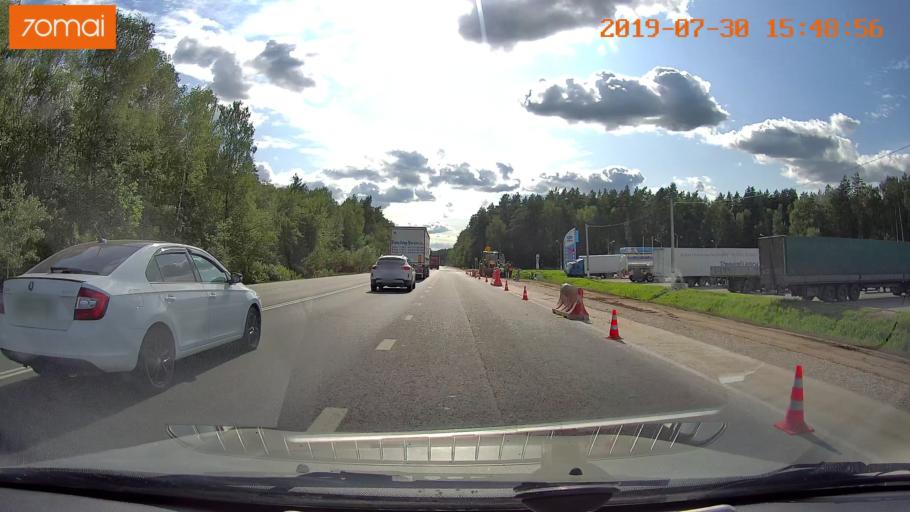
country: RU
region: Moskovskaya
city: Voskresensk
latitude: 55.3400
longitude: 38.6749
